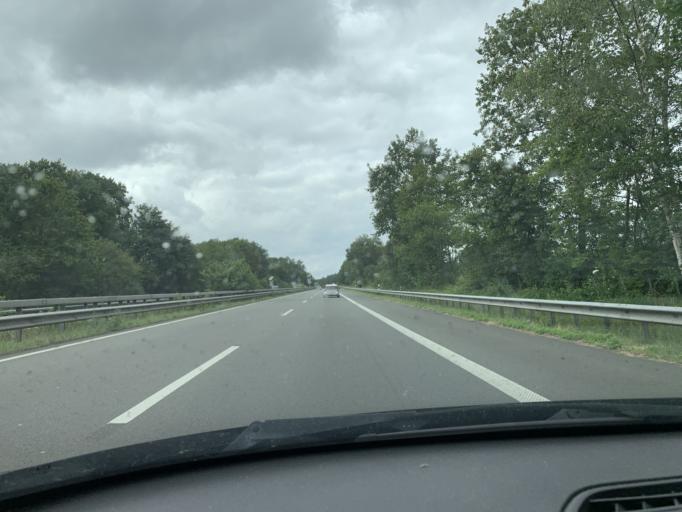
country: DE
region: Lower Saxony
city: Bad Zwischenahn
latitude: 53.2313
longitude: 8.0329
